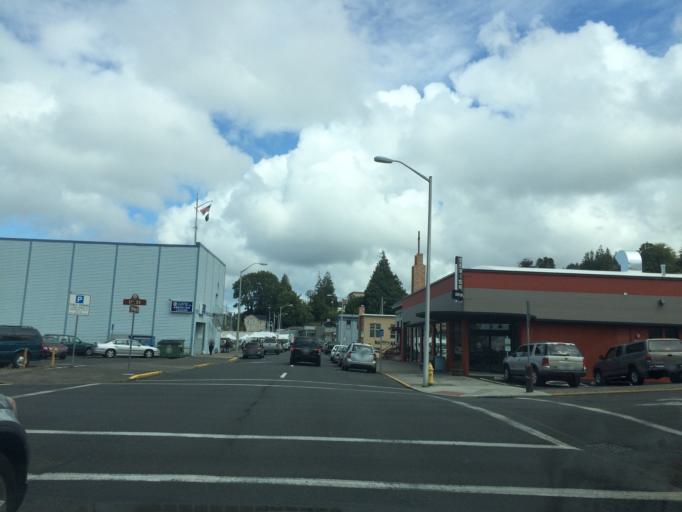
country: US
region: Oregon
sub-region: Clatsop County
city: Astoria
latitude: 46.1877
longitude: -123.8321
